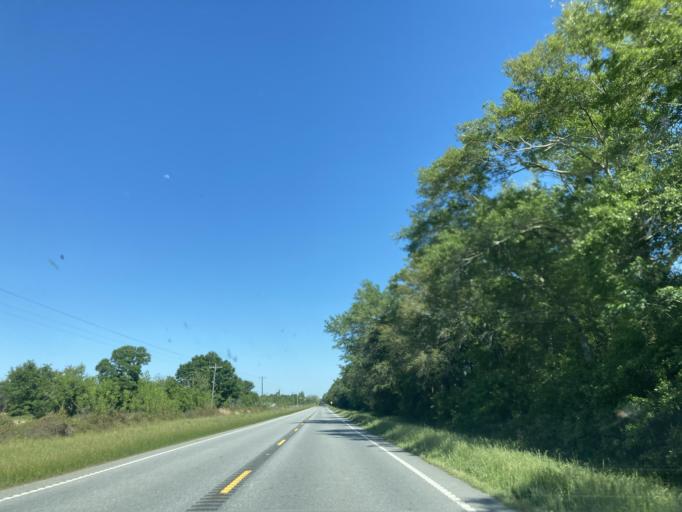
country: US
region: Georgia
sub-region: Miller County
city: Colquitt
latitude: 31.1838
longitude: -84.5586
